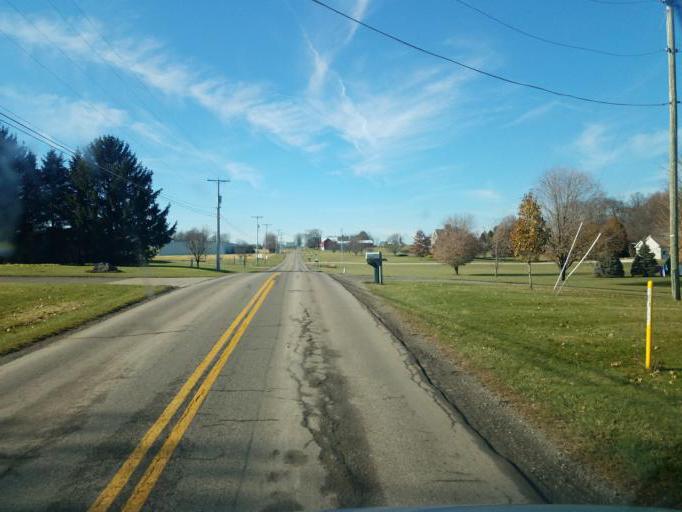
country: US
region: Ohio
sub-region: Wayne County
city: Apple Creek
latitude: 40.7412
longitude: -81.7580
